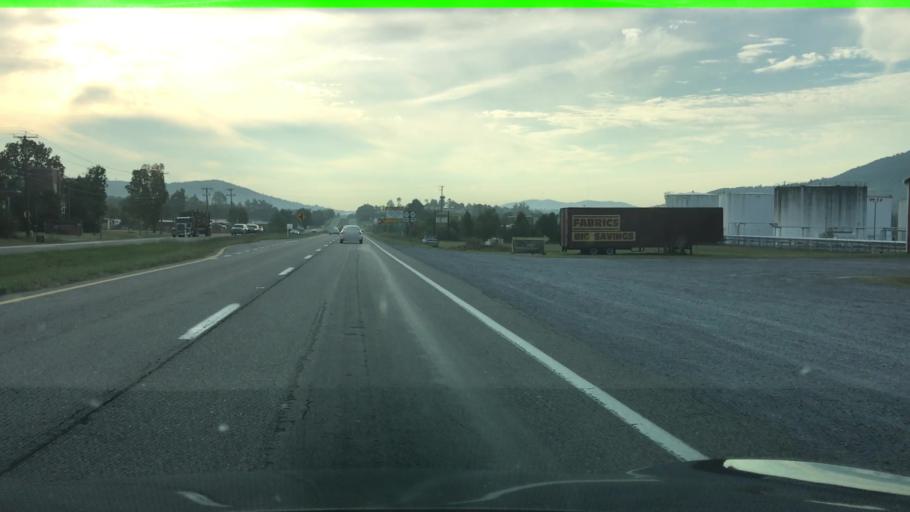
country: US
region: Virginia
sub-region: Botetourt County
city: Blue Ridge
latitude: 37.3852
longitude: -79.7340
